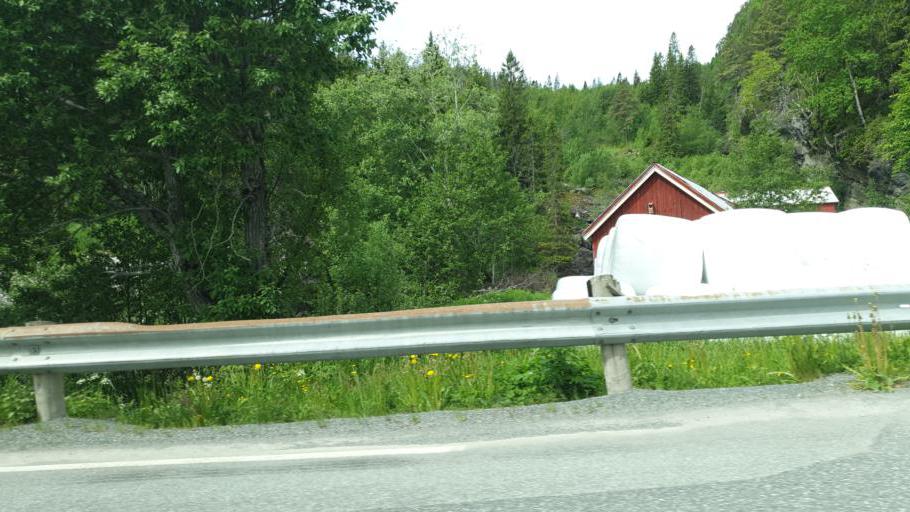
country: NO
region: Nord-Trondelag
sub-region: Leksvik
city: Leksvik
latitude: 63.5999
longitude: 10.4584
